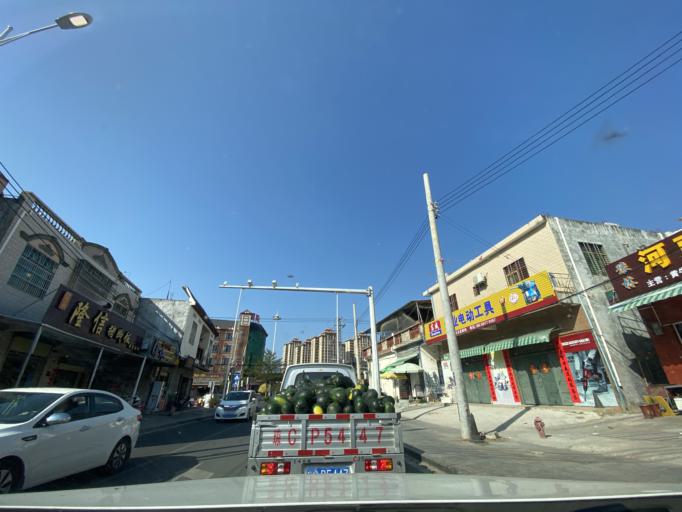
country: CN
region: Hainan
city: Yingzhou
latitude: 18.4224
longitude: 109.8550
